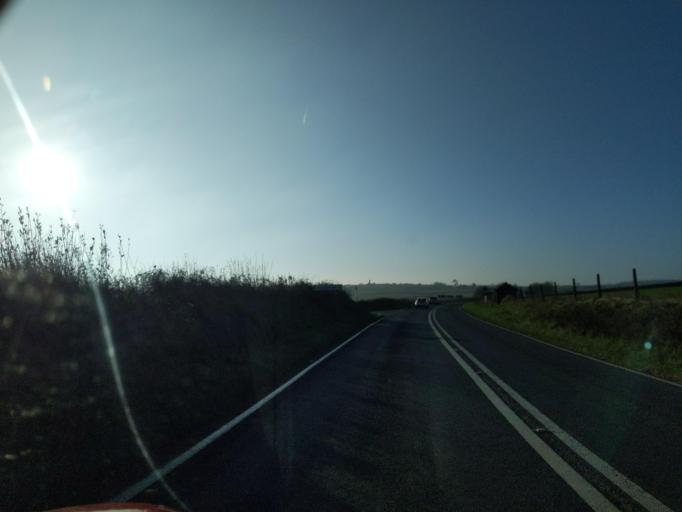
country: GB
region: England
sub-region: Cornwall
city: Liskeard
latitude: 50.4516
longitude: -4.5412
